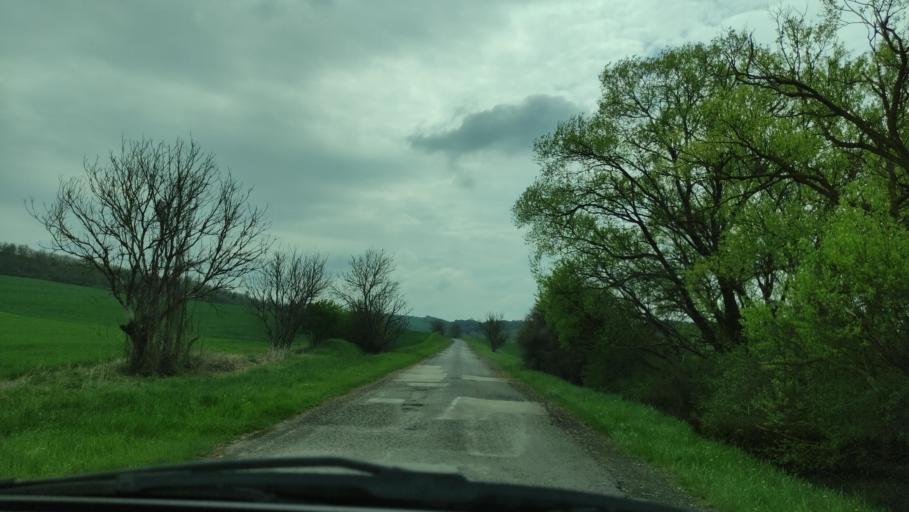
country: HU
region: Baranya
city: Magocs
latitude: 46.3055
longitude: 18.1897
